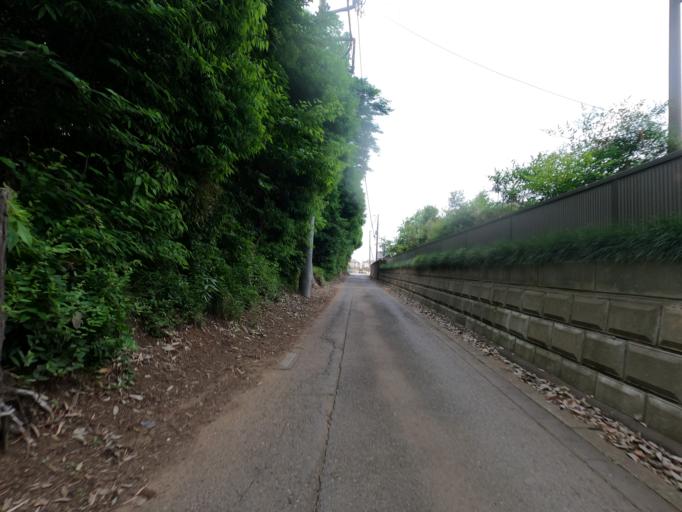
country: JP
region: Ibaraki
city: Moriya
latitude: 35.9541
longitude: 139.9693
